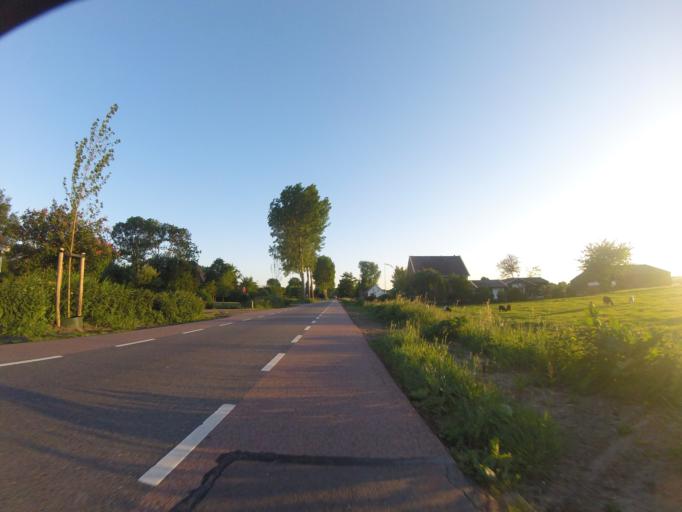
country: NL
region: North Holland
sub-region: Gemeente Haarlemmermeer
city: Hoofddorp
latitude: 52.3617
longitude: 4.6938
